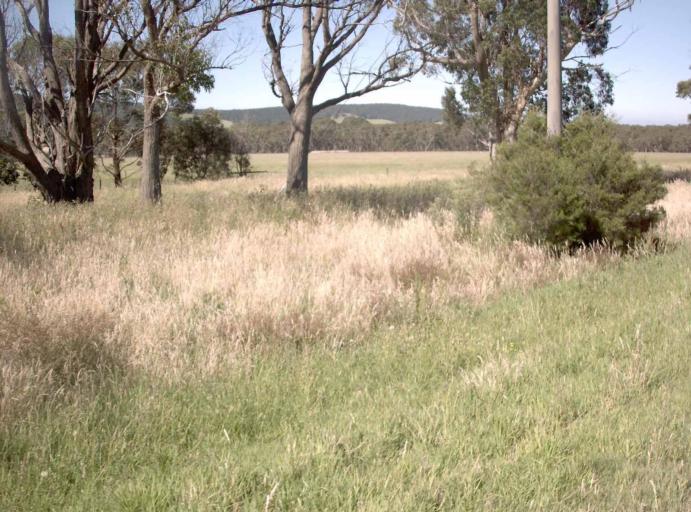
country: AU
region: Victoria
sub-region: Latrobe
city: Morwell
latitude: -38.6415
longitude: 146.4869
